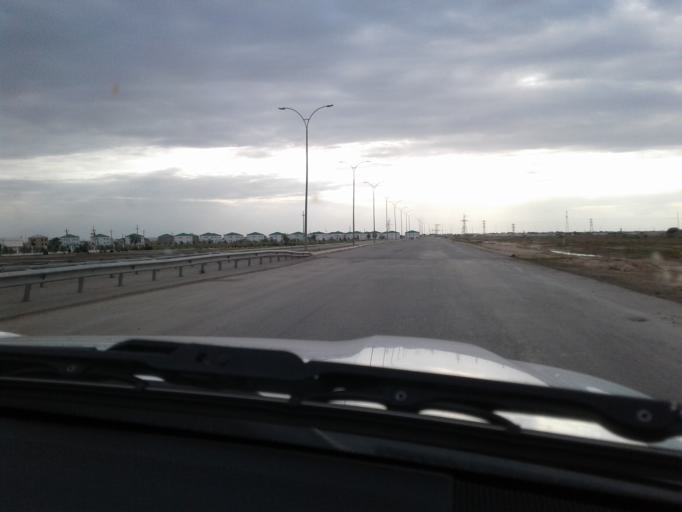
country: TM
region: Ahal
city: Tejen
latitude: 37.3645
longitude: 60.5369
